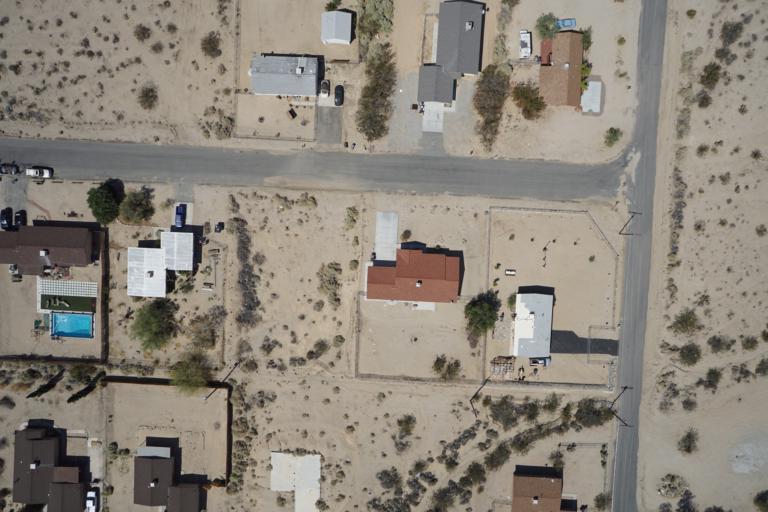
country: US
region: California
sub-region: San Bernardino County
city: Twentynine Palms
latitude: 34.1281
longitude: -116.0343
